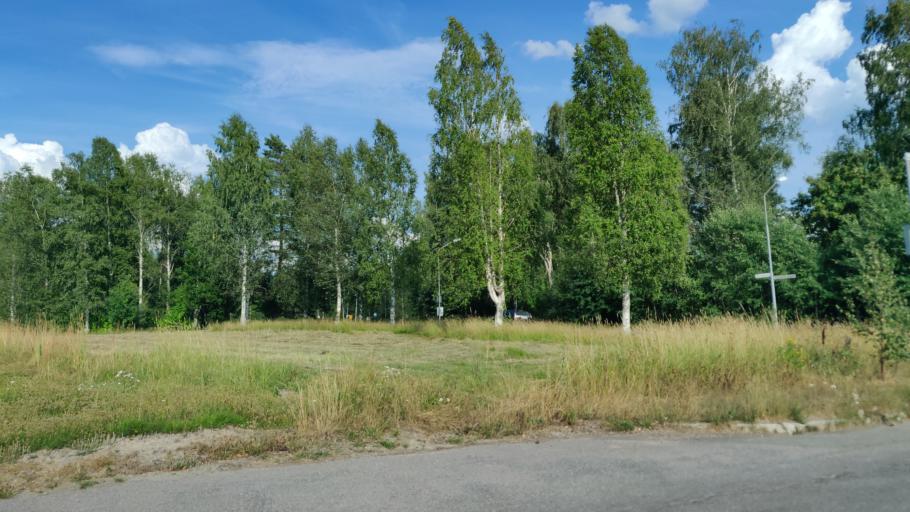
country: SE
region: Vaermland
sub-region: Hagfors Kommun
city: Hagfors
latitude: 60.0465
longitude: 13.6702
